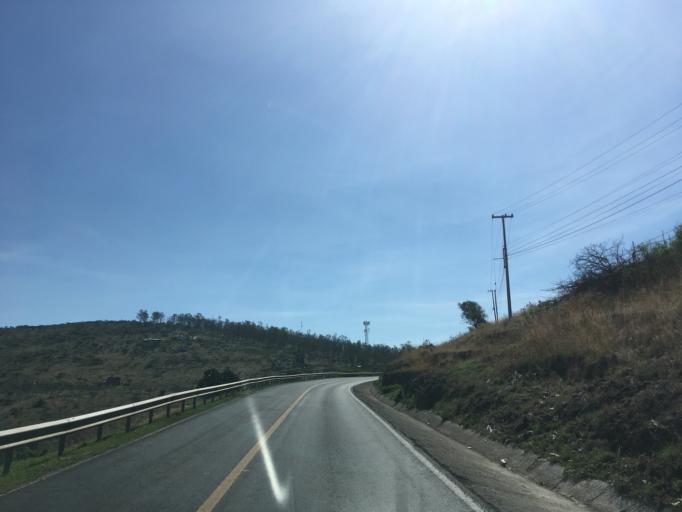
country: MX
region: Michoacan
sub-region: Morelia
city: Puerto de Buenavista (Lazaro Cardenas)
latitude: 19.6885
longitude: -101.1035
